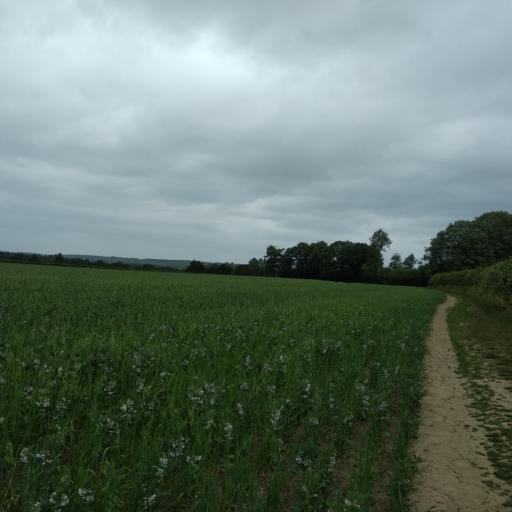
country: GB
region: England
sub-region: Kent
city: Ashford
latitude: 51.1615
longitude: 0.8296
